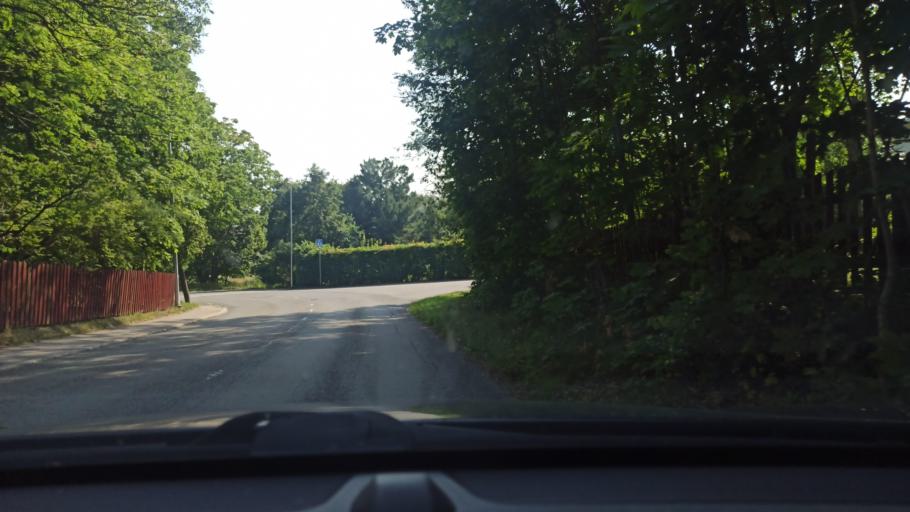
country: FI
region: Varsinais-Suomi
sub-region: Turku
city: Turku
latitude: 60.4604
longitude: 22.2317
